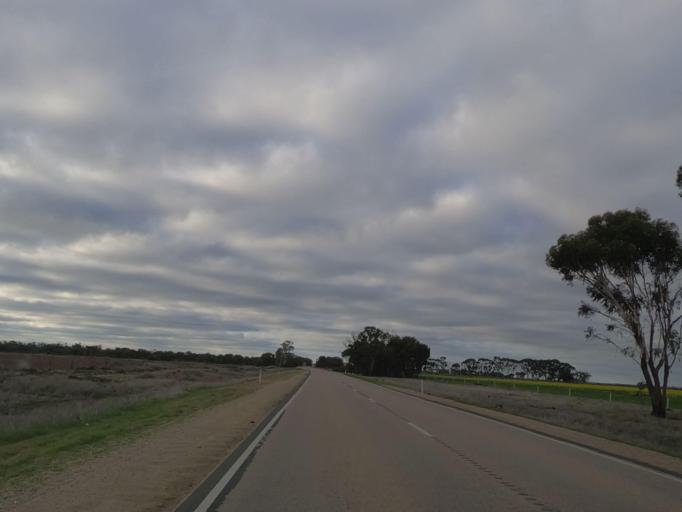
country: AU
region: Victoria
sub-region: Swan Hill
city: Swan Hill
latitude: -35.8251
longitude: 143.9475
